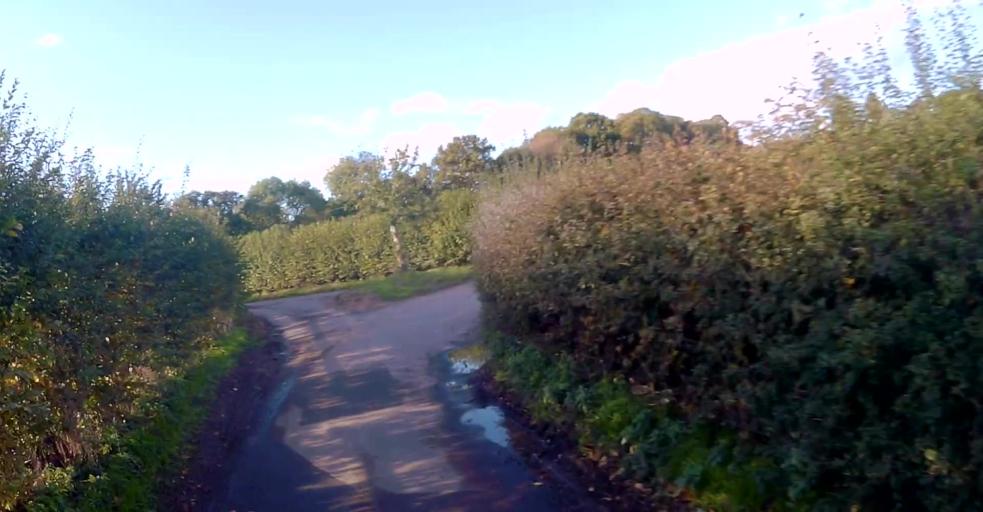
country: GB
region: England
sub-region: Surrey
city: Farnham
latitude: 51.2121
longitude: -0.8565
